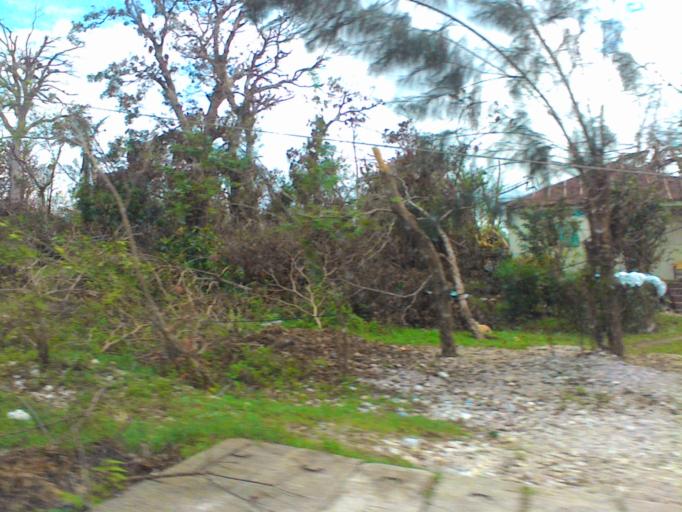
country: HT
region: Sud
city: Chantal
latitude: 18.3337
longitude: -73.8461
